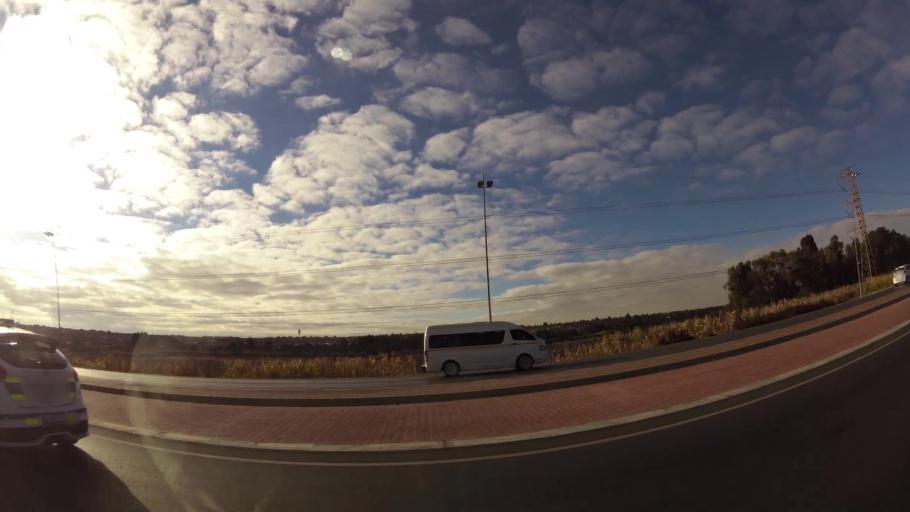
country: ZA
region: Gauteng
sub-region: City of Johannesburg Metropolitan Municipality
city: Modderfontein
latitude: -26.0424
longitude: 28.1884
